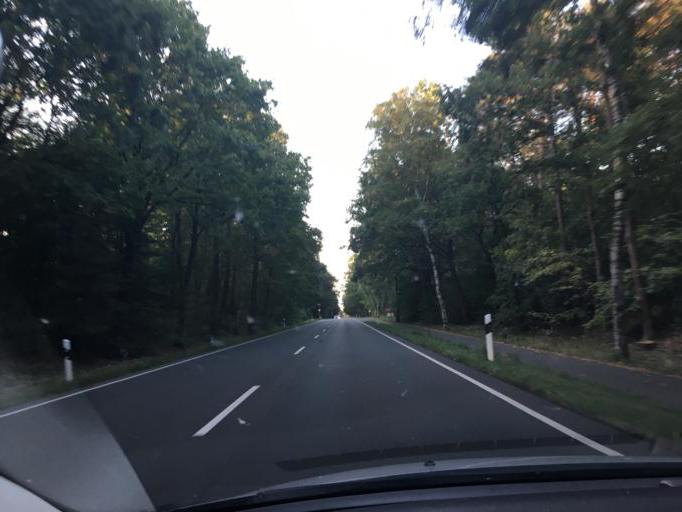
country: DE
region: Lower Saxony
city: Wietzendorf
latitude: 52.8741
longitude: 9.9143
